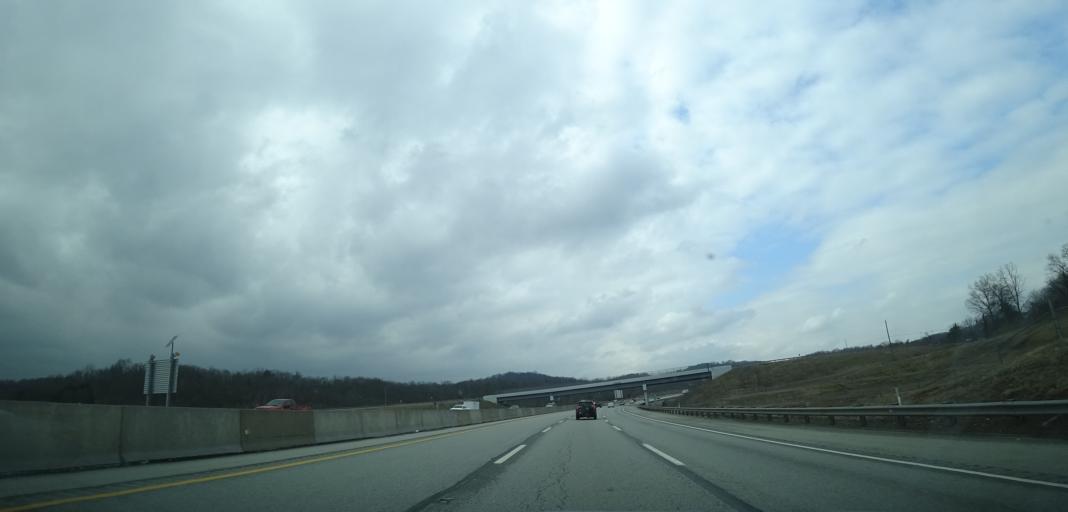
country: US
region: Pennsylvania
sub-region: Westmoreland County
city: New Stanton
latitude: 40.2419
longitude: -79.6341
